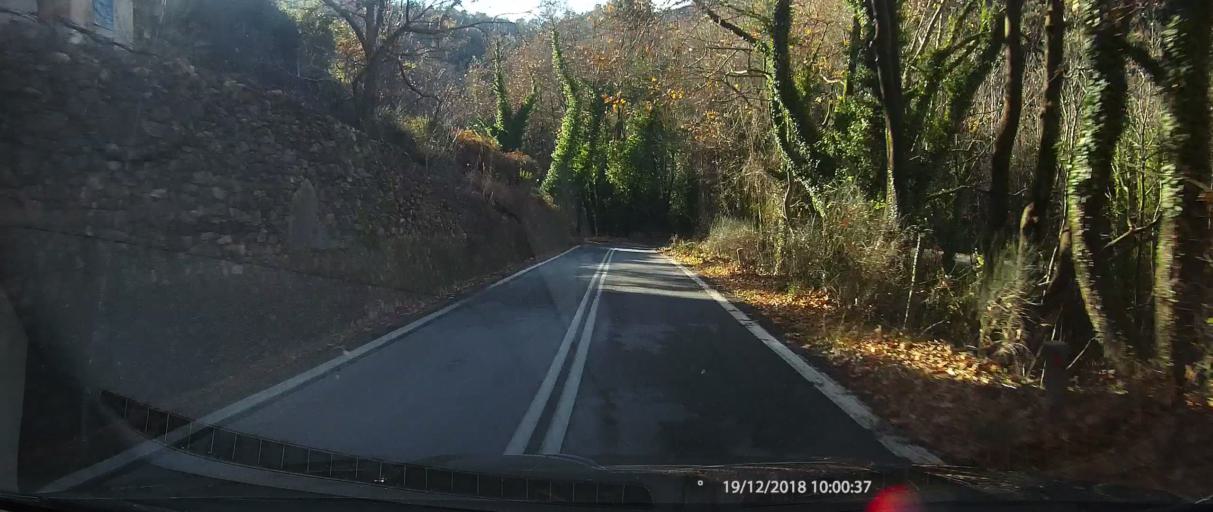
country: GR
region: Peloponnese
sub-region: Nomos Messinias
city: Paralia Vergas
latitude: 37.0927
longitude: 22.2331
